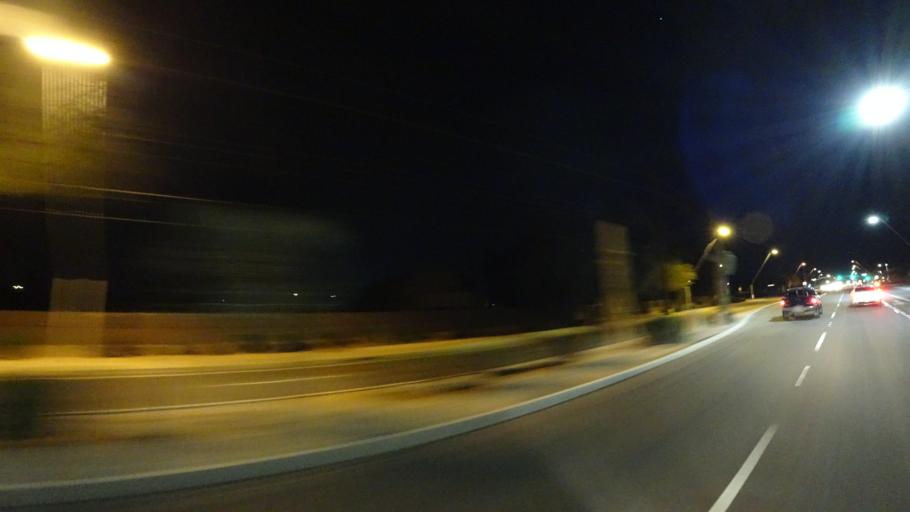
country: US
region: Arizona
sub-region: Maricopa County
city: Chandler
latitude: 33.3016
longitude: -111.8243
